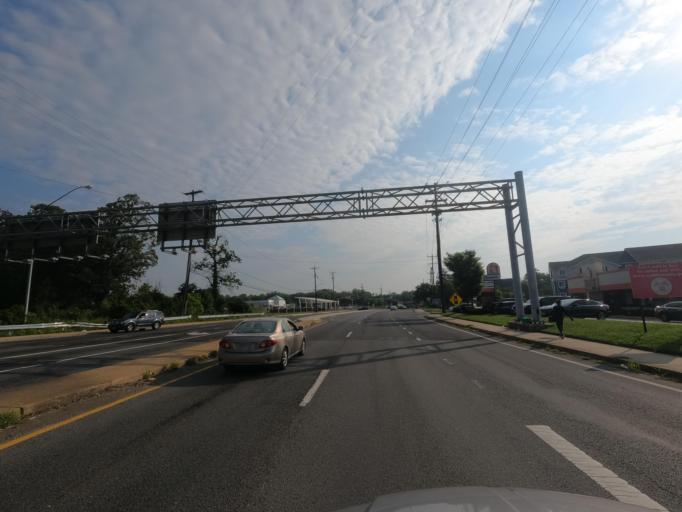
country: US
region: Maryland
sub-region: Prince George's County
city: Camp Springs
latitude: 38.8054
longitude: -76.9053
